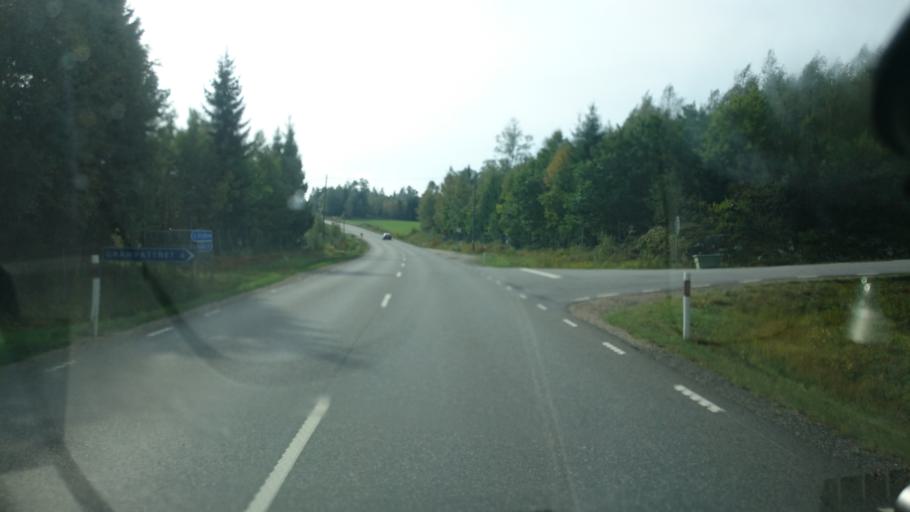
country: SE
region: Vaestra Goetaland
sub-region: Alingsas Kommun
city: Alingsas
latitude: 58.0064
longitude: 12.4440
